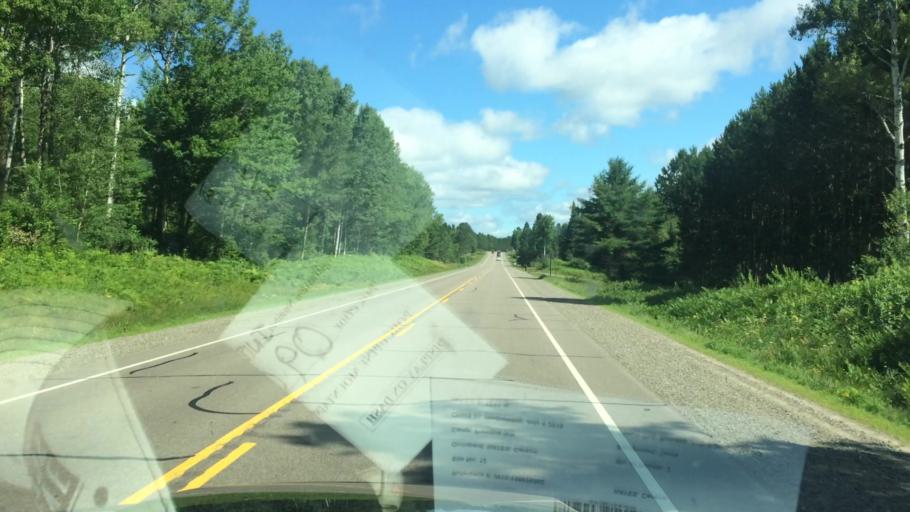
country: US
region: Wisconsin
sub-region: Oneida County
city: Rhinelander
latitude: 45.5824
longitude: -89.5694
